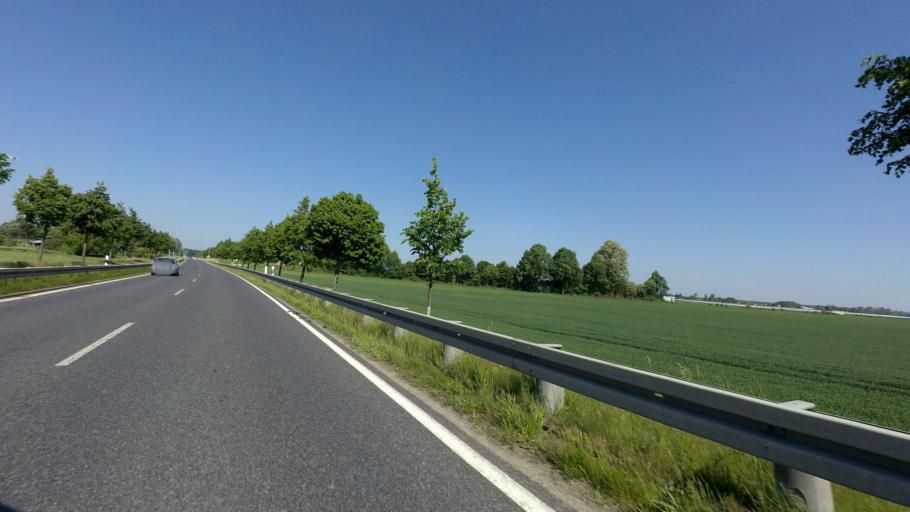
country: DE
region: Saxony
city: Kamenz
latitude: 51.2875
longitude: 14.1250
